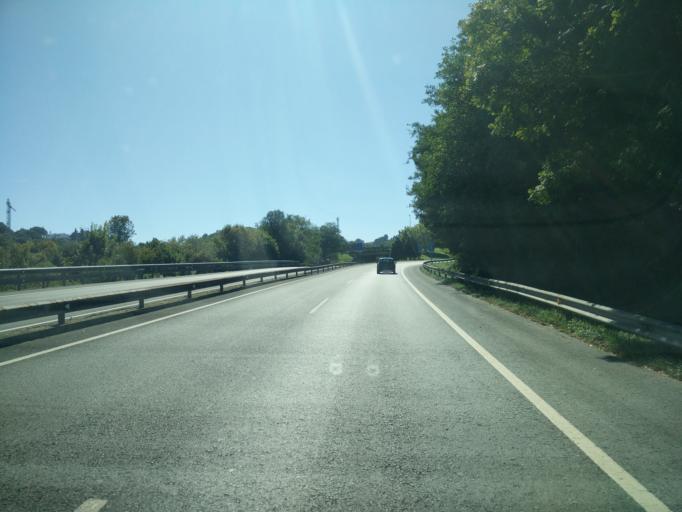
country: ES
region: Basque Country
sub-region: Provincia de Guipuzcoa
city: San Sebastian
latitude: 43.3005
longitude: -2.0071
